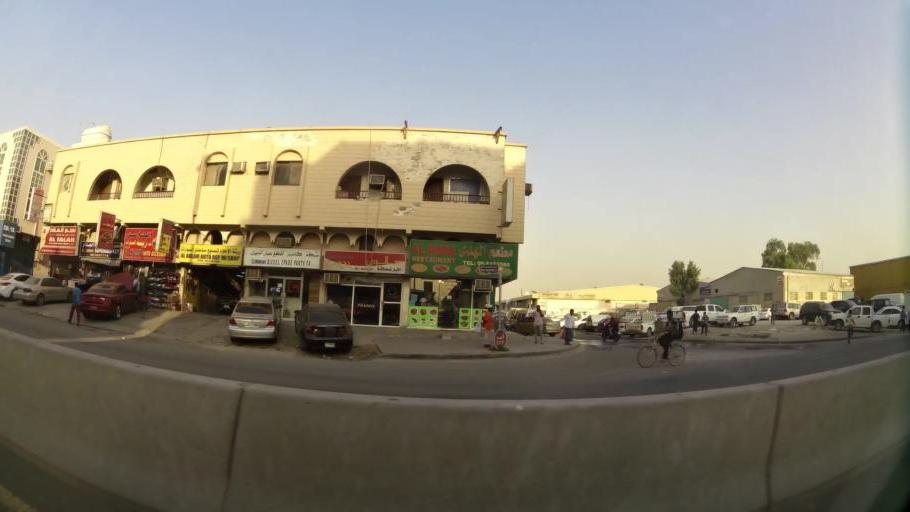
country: AE
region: Ash Shariqah
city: Sharjah
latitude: 25.3278
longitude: 55.4077
